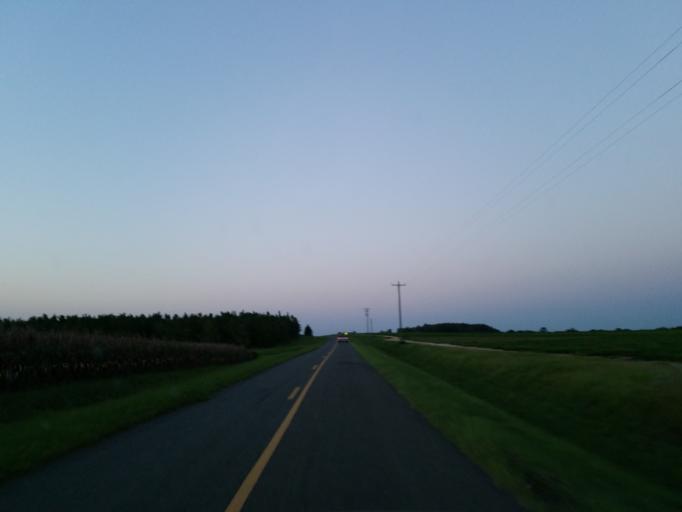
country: US
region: Georgia
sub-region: Dooly County
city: Unadilla
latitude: 32.2865
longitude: -83.7925
